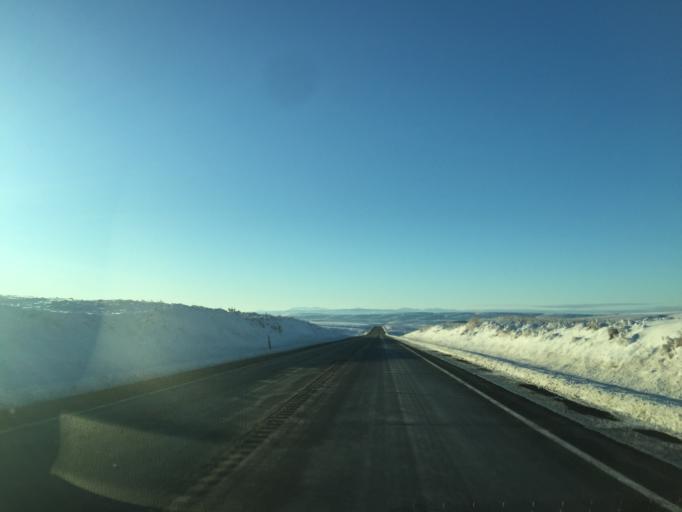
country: US
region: Washington
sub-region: Grant County
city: Soap Lake
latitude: 47.5994
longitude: -119.5929
